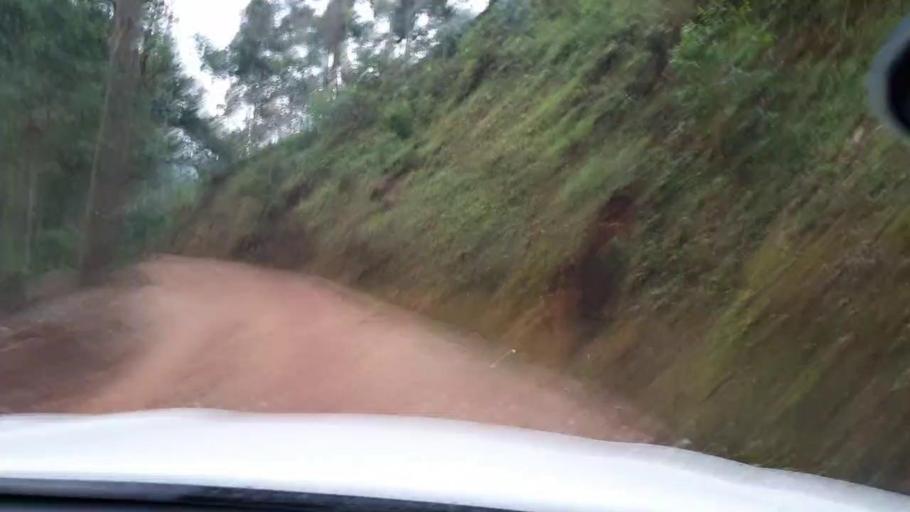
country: RW
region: Western Province
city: Cyangugu
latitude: -2.4084
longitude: 29.2053
